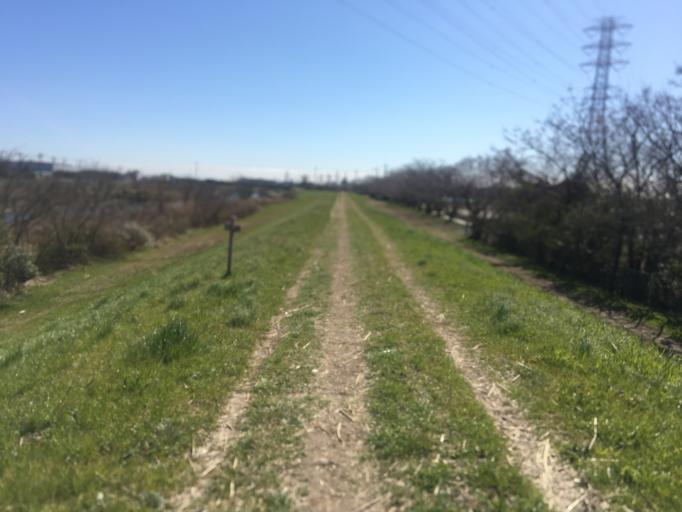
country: JP
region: Saitama
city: Asaka
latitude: 35.8227
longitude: 139.6033
